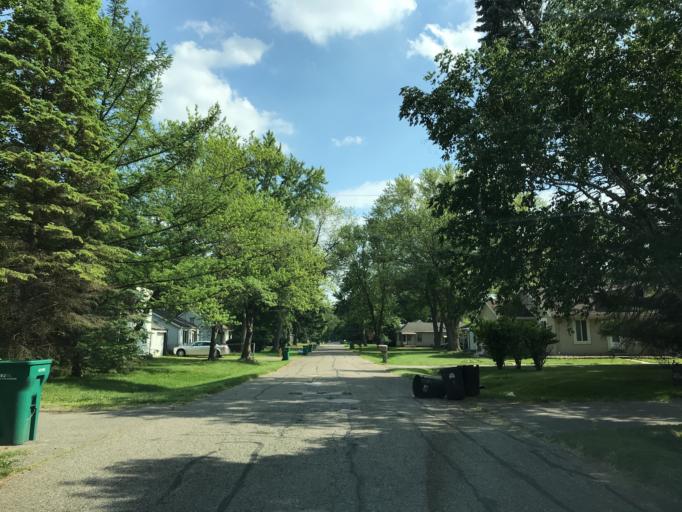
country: US
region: Michigan
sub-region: Oakland County
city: Farmington
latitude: 42.4519
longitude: -83.3300
